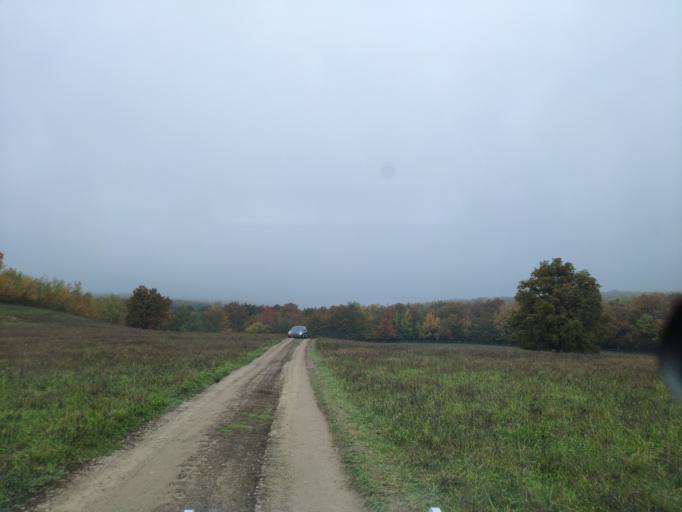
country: SK
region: Kosicky
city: Moldava nad Bodvou
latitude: 48.7134
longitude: 21.0134
